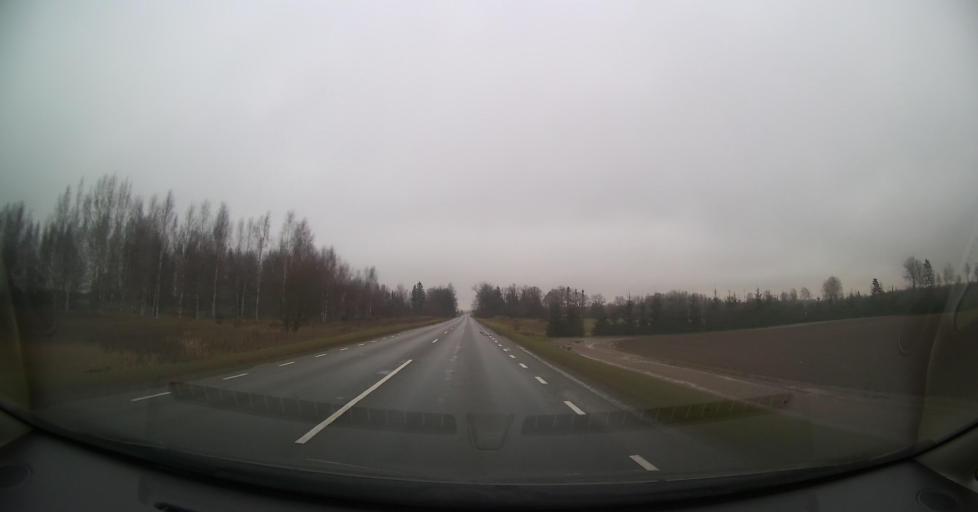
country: EE
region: Tartu
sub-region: Tartu linn
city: Tartu
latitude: 58.3659
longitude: 26.9072
